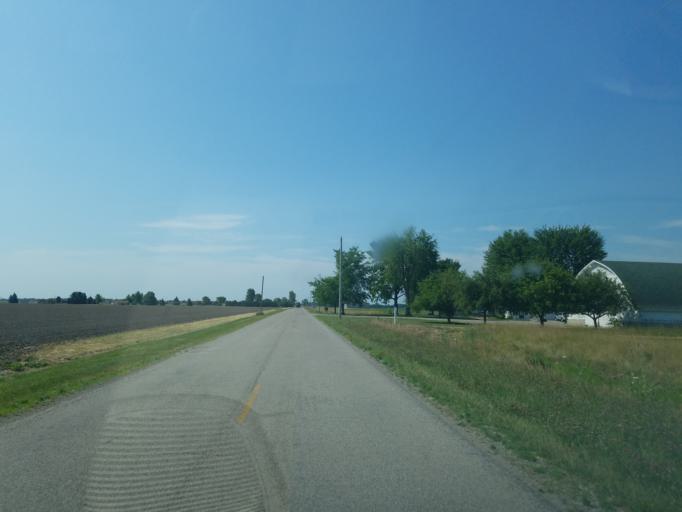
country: US
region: Ohio
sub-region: Van Wert County
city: Van Wert
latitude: 40.9083
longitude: -84.6295
